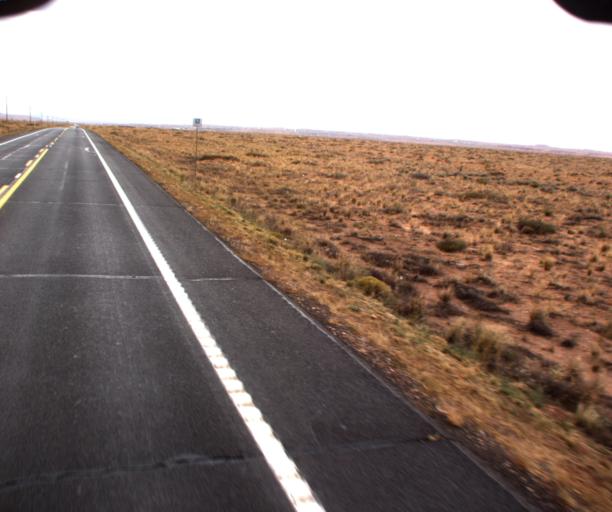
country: US
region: Arizona
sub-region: Coconino County
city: Tuba City
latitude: 36.1409
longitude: -111.1606
